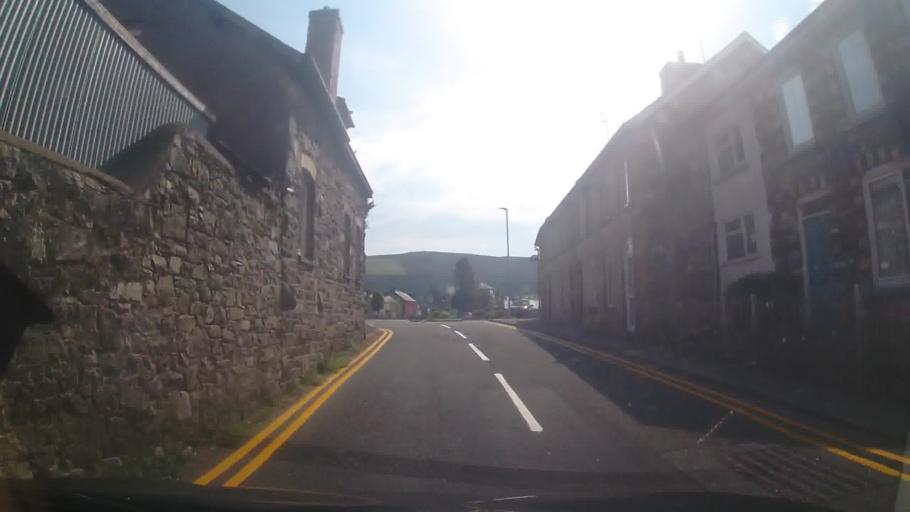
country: GB
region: Wales
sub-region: Sir Powys
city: Rhayader
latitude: 52.3021
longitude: -3.5128
